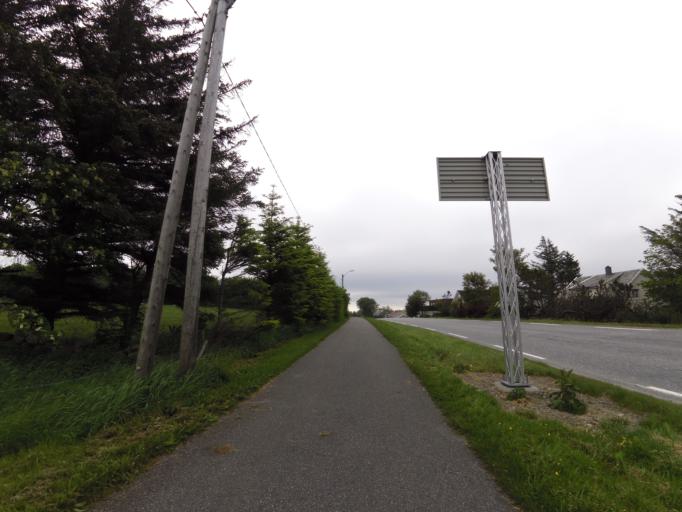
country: NO
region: Rogaland
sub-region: Ha
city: Vigrestad
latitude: 58.5743
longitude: 5.6788
